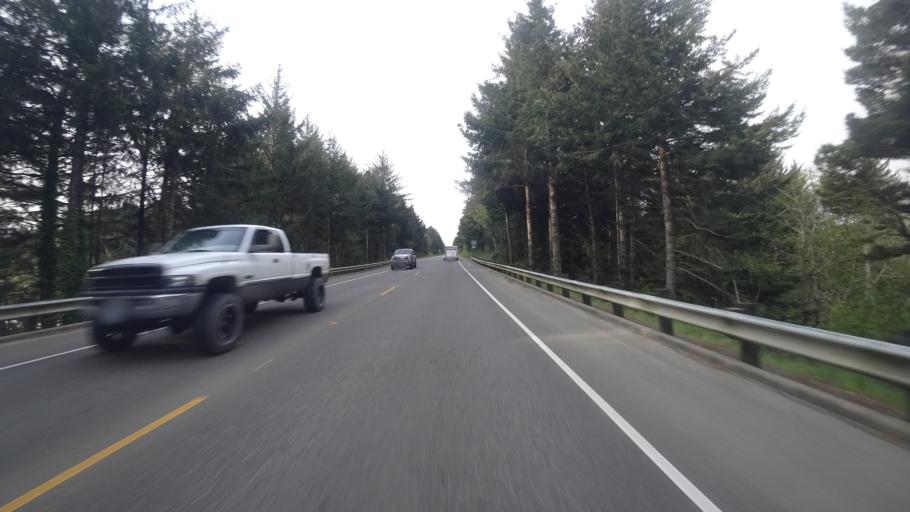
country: US
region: Oregon
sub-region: Coos County
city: Bandon
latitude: 43.1329
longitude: -124.3981
